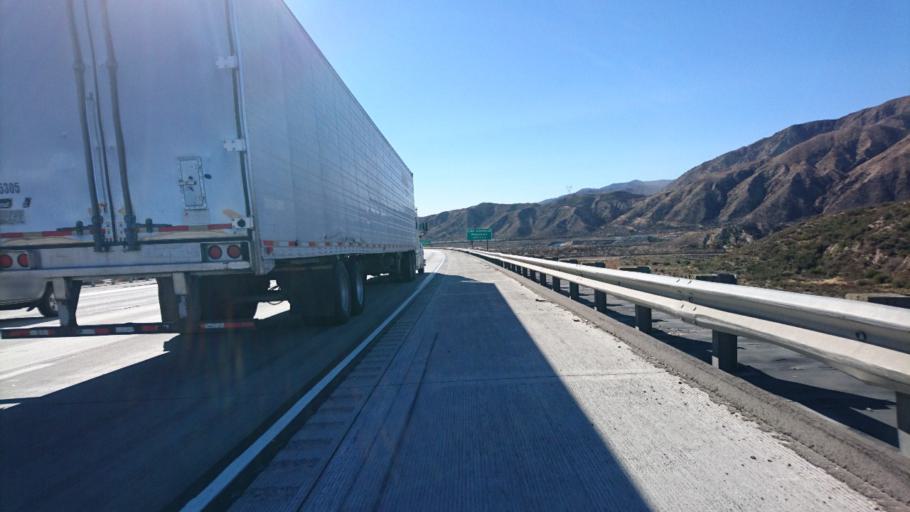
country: US
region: California
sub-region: San Bernardino County
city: Oak Hills
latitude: 34.3226
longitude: -117.4823
